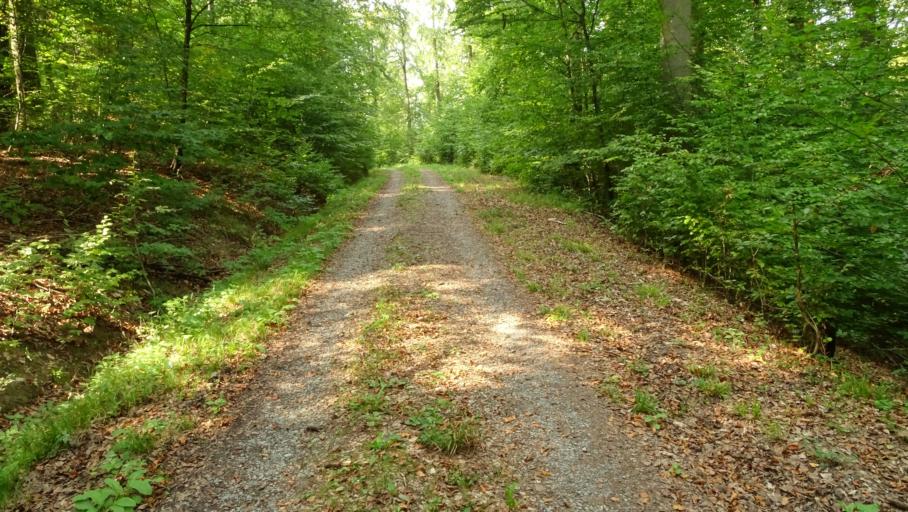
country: DE
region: Baden-Wuerttemberg
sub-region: Karlsruhe Region
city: Mosbach
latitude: 49.3817
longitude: 9.1205
